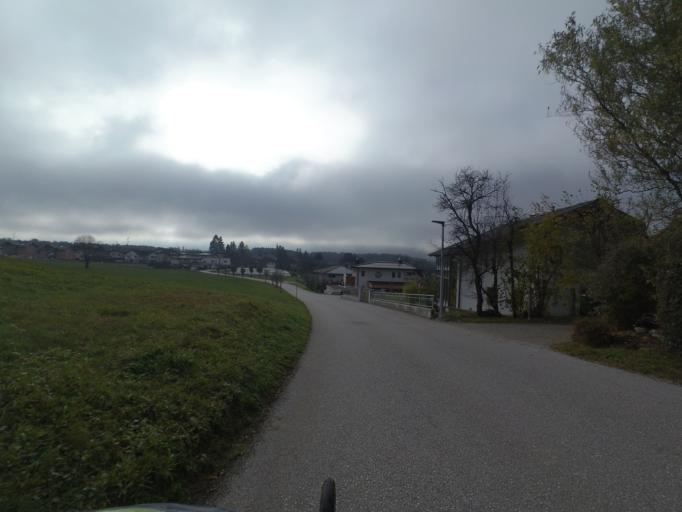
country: AT
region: Salzburg
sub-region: Politischer Bezirk Hallein
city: Adnet
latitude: 47.6683
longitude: 13.1368
